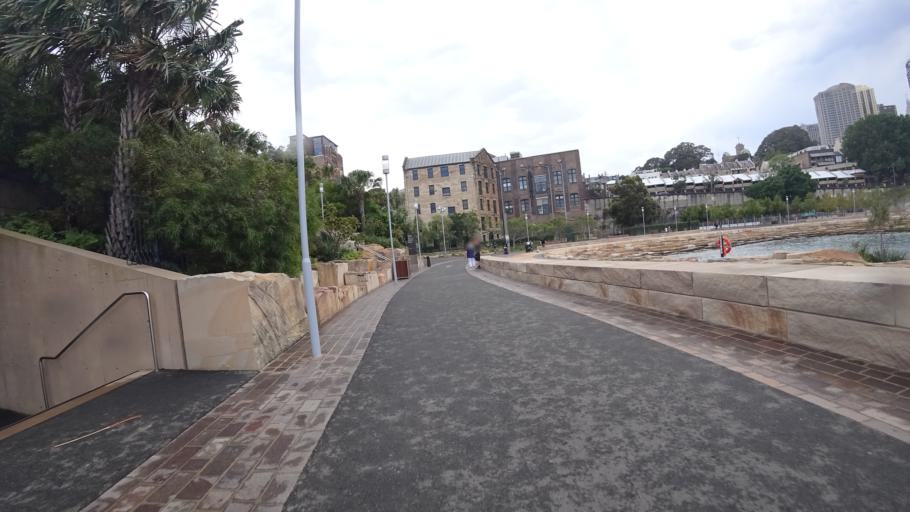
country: AU
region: New South Wales
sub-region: Leichhardt
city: Balmain East
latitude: -33.8586
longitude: 151.2013
